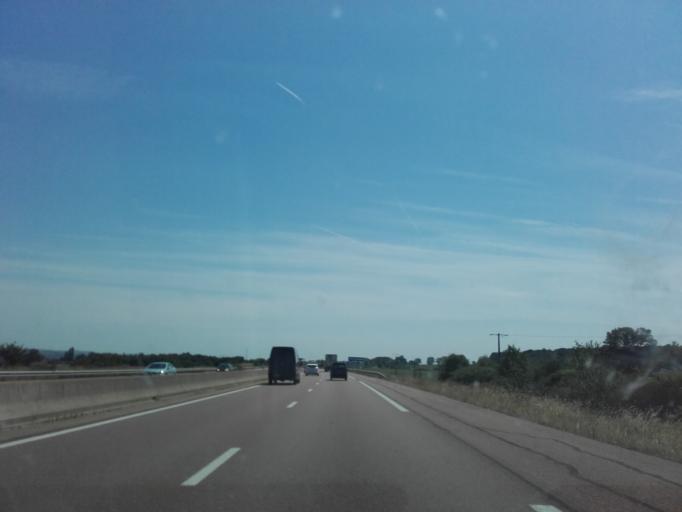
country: FR
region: Bourgogne
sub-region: Departement de l'Yonne
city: Avallon
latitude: 47.5036
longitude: 4.0248
